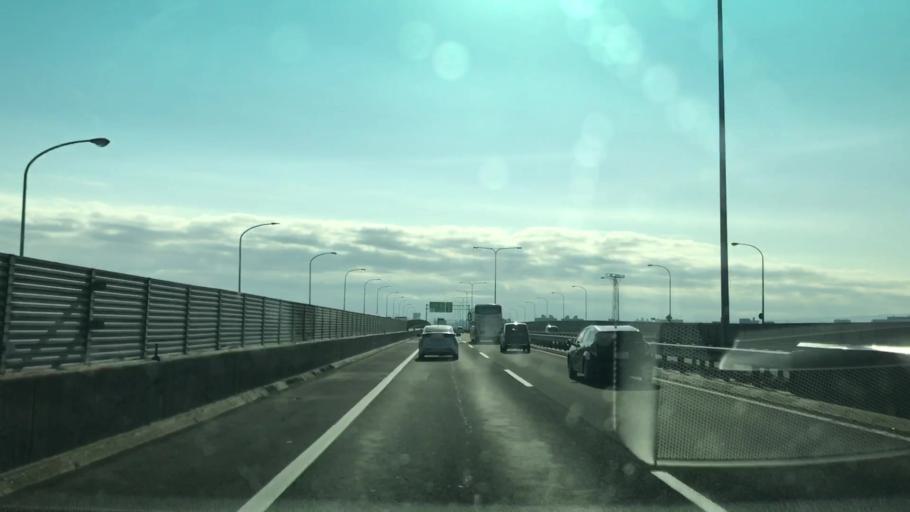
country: JP
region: Hokkaido
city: Sapporo
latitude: 43.0489
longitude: 141.4327
